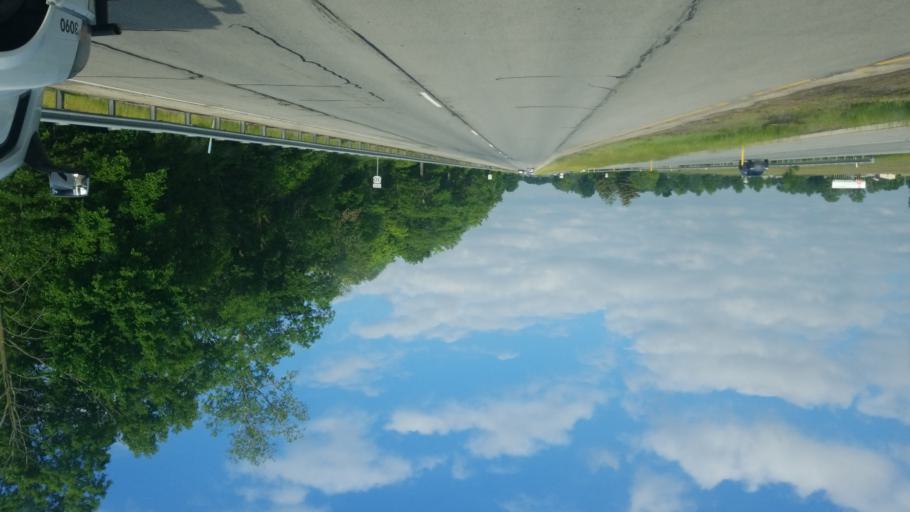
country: US
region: Indiana
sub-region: Whitley County
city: Churubusco
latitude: 41.1258
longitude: -85.2992
